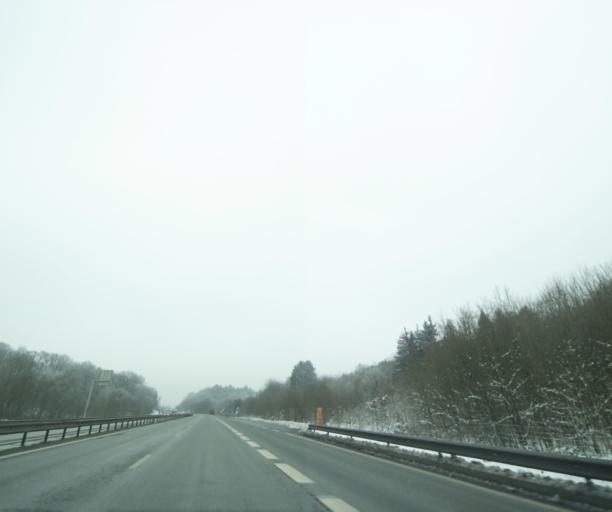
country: FR
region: Rhone-Alpes
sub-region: Departement de l'Ain
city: Poncin
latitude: 46.1020
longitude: 5.4381
